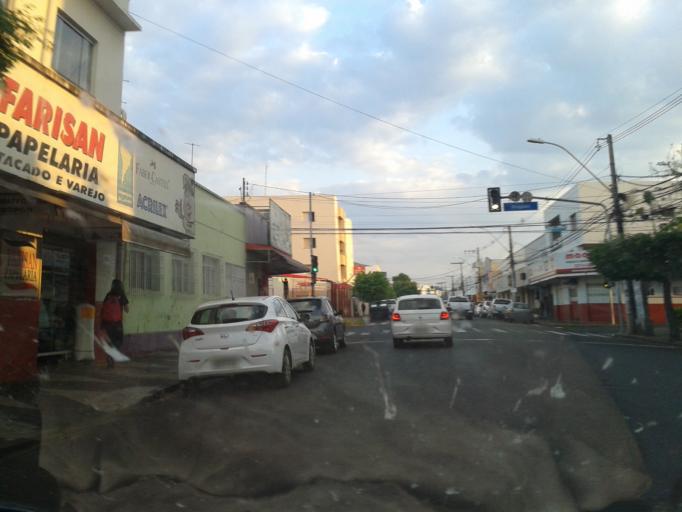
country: BR
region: Minas Gerais
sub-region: Uberlandia
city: Uberlandia
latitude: -18.9076
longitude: -48.2782
